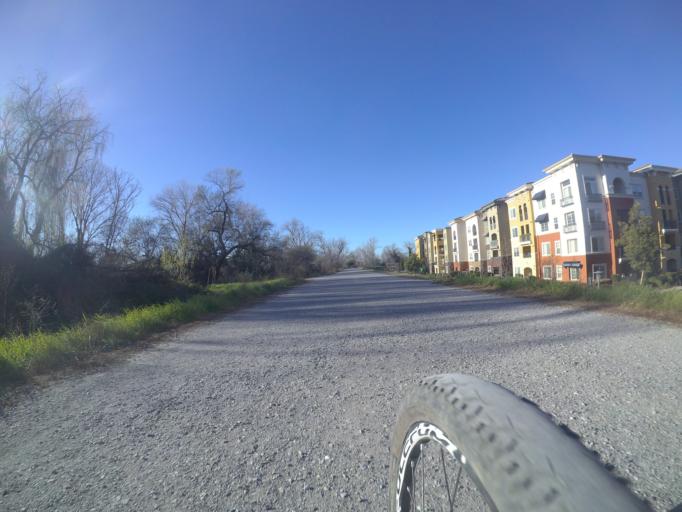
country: US
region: California
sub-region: Santa Clara County
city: Milpitas
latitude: 37.4166
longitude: -121.9285
